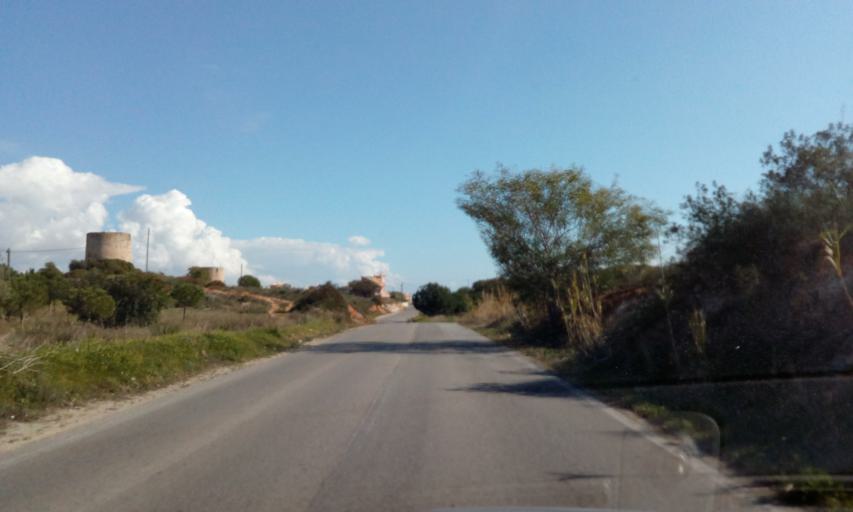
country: PT
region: Faro
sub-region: Albufeira
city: Ferreiras
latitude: 37.1189
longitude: -8.2170
